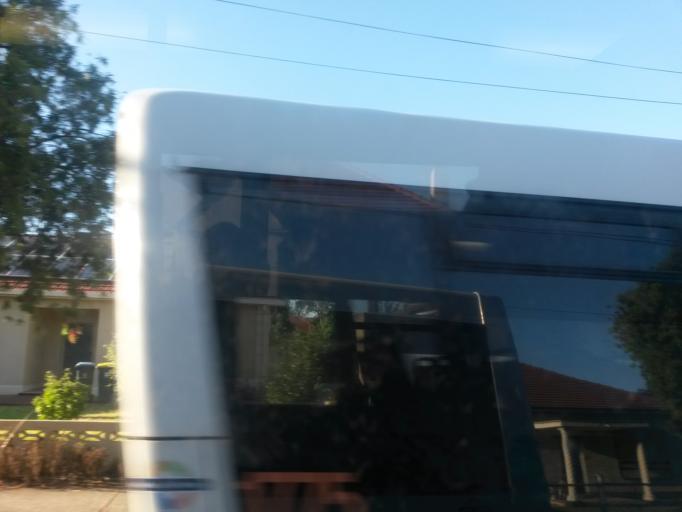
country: AU
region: South Australia
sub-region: Charles Sturt
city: Woodville
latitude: -34.8825
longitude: 138.5701
